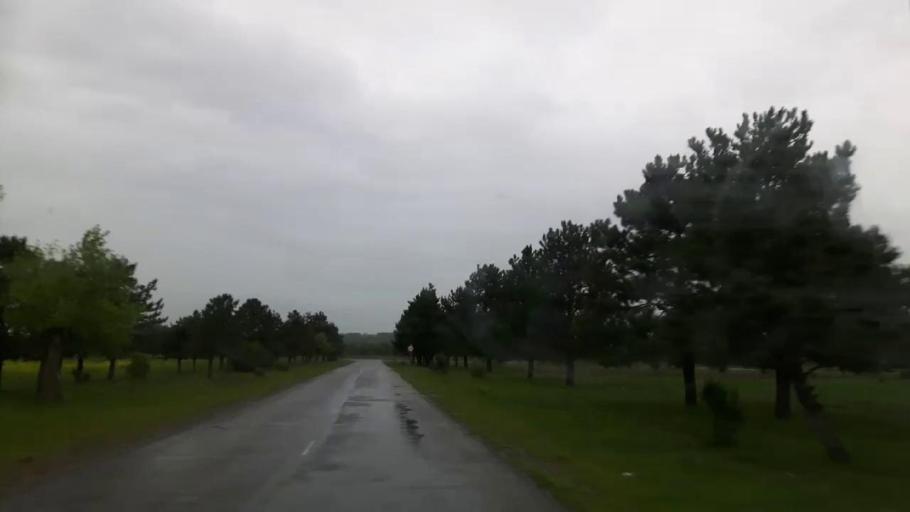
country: GE
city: Agara
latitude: 42.0190
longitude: 43.9064
